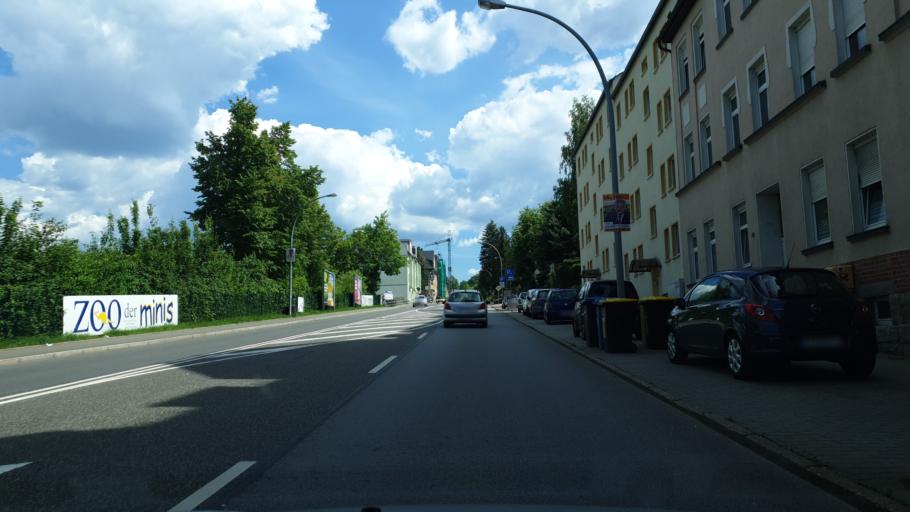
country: DE
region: Saxony
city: Aue
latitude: 50.5831
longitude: 12.7098
